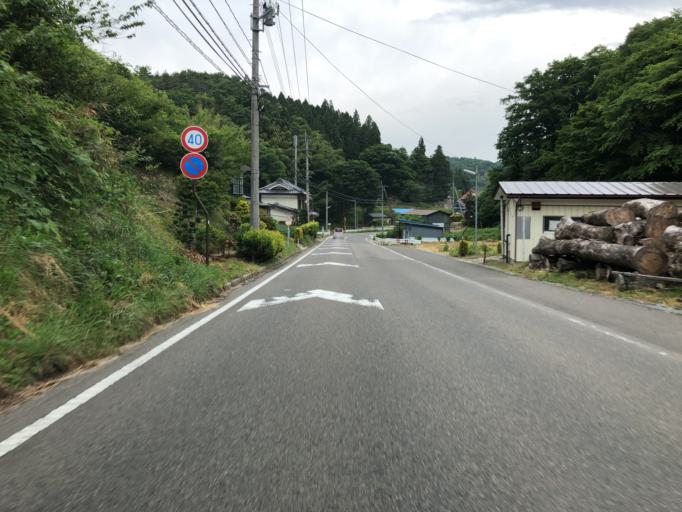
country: JP
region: Fukushima
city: Miharu
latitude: 37.4526
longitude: 140.5167
